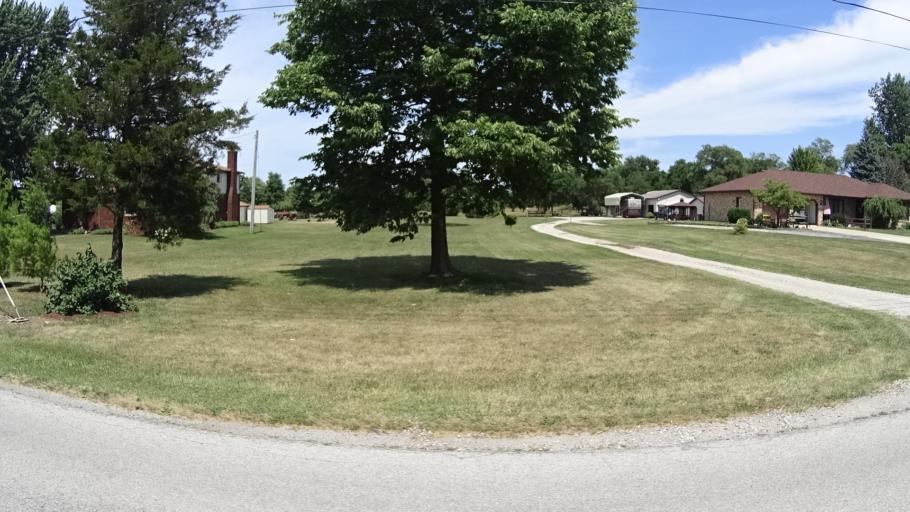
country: US
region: Ohio
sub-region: Erie County
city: Sandusky
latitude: 41.3935
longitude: -82.7956
